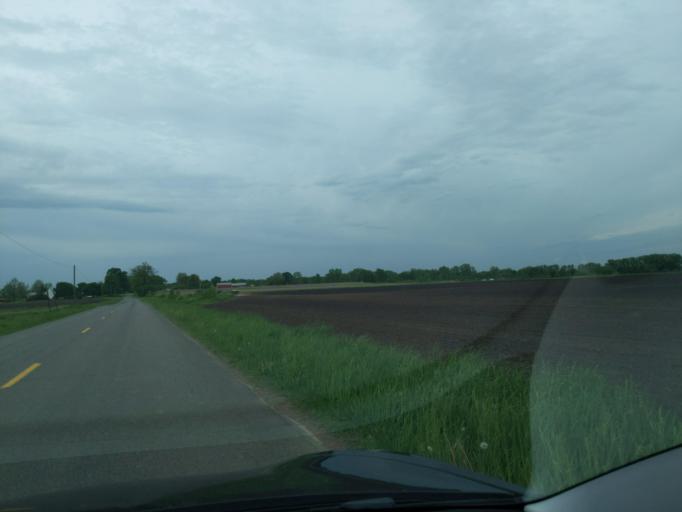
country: US
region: Michigan
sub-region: Ingham County
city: Stockbridge
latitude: 42.4257
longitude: -84.2142
